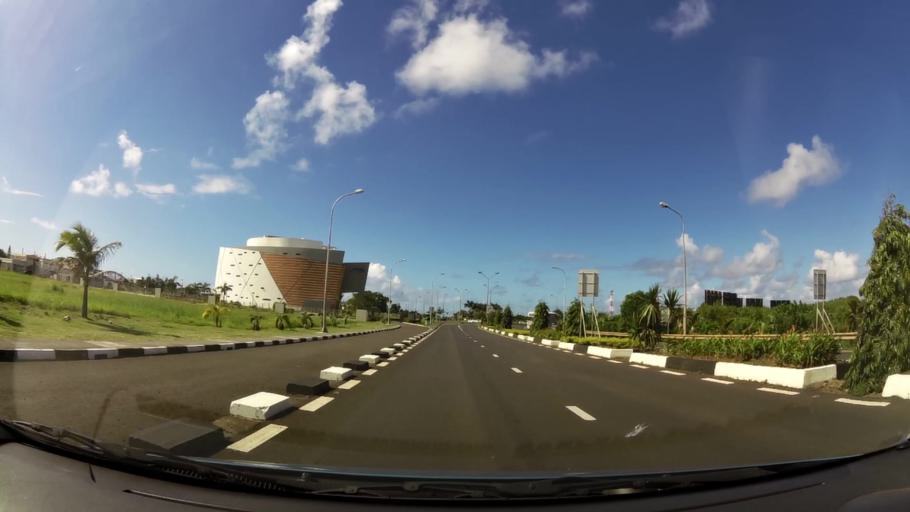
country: MU
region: Grand Port
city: Plaine Magnien
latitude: -20.4336
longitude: 57.6726
